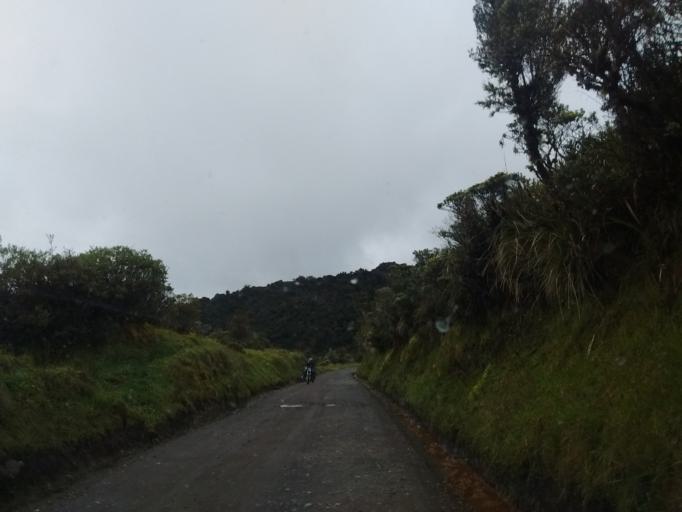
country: CO
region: Cauca
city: Totoro
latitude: 2.3567
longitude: -76.3310
